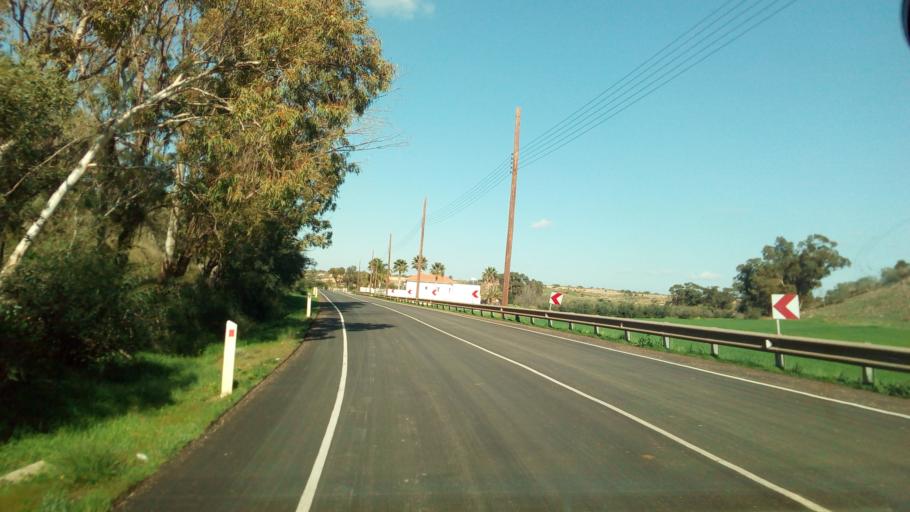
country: CY
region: Ammochostos
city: Avgorou
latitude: 35.0576
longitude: 33.8380
